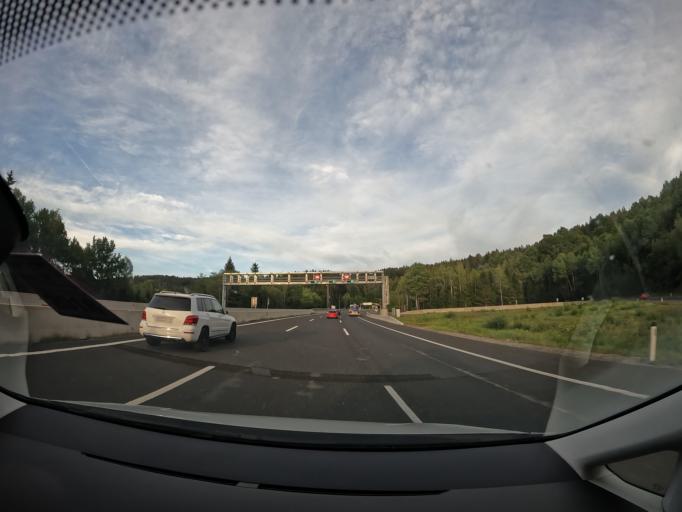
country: AT
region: Carinthia
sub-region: Politischer Bezirk Wolfsberg
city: Bad Sankt Leonhard im Lavanttal
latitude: 46.9410
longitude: 14.8418
